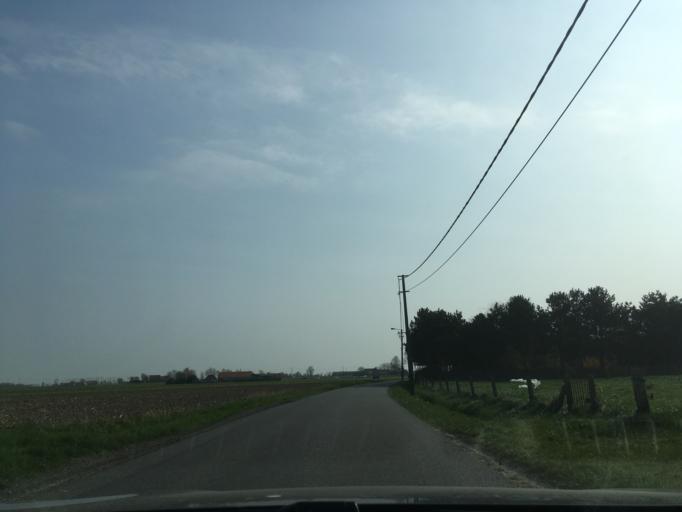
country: BE
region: Flanders
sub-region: Provincie West-Vlaanderen
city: Lichtervelde
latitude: 51.0194
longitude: 3.1824
